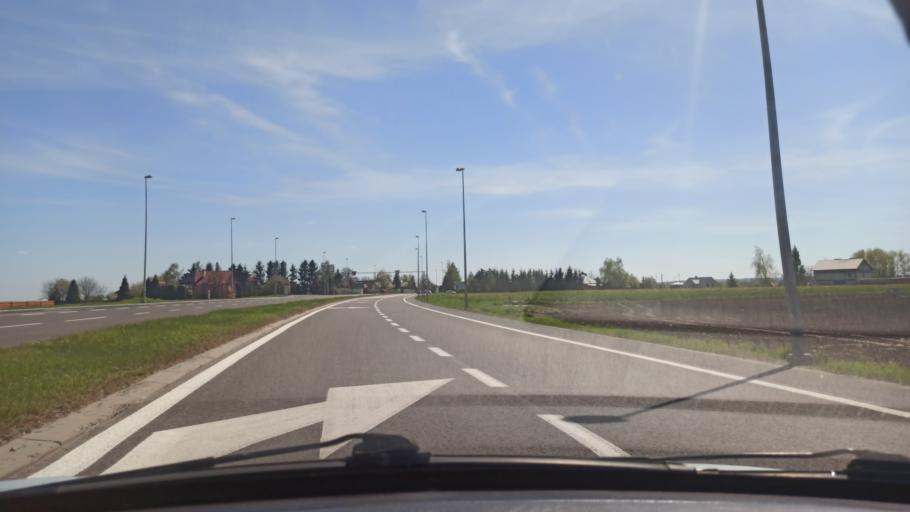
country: PL
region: Subcarpathian Voivodeship
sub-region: Powiat jaroslawski
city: Radymno
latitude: 49.9301
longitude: 22.8214
